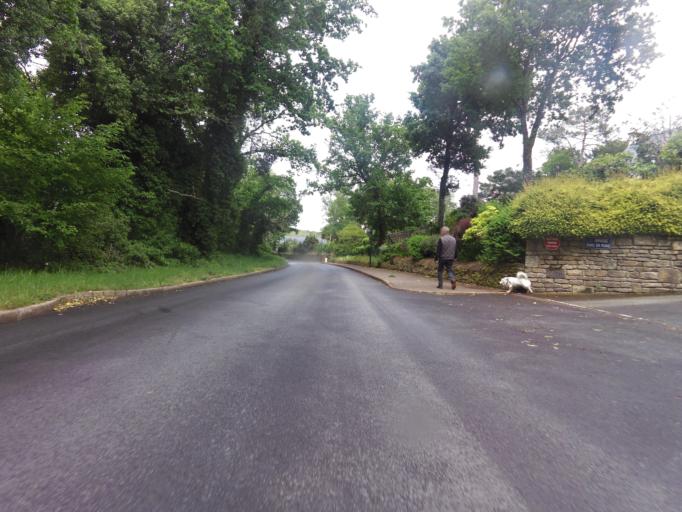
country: FR
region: Brittany
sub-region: Departement du Morbihan
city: Baden
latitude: 47.6201
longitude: -2.9218
